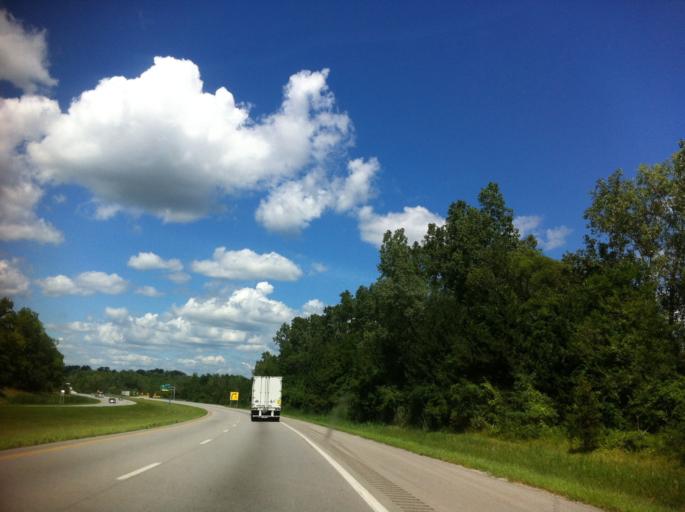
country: US
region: Ohio
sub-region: Lucas County
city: Sylvania
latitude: 41.7064
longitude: -83.6891
